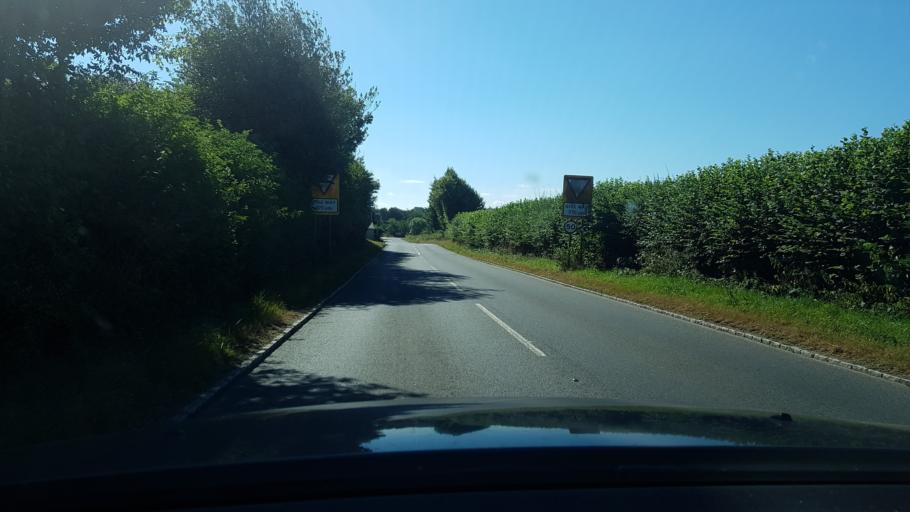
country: GB
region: England
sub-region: West Berkshire
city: Wickham
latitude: 51.4591
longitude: -1.4818
